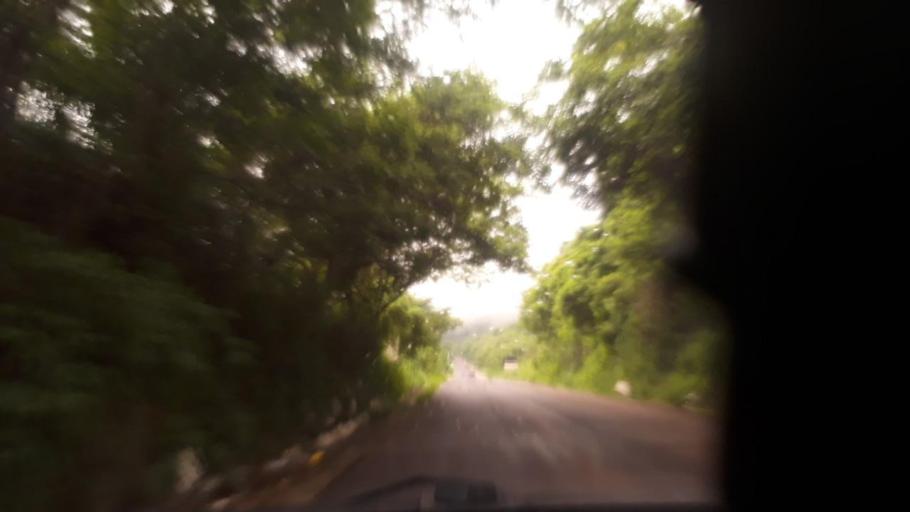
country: GT
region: Jutiapa
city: Jalpatagua
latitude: 14.1700
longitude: -90.0442
